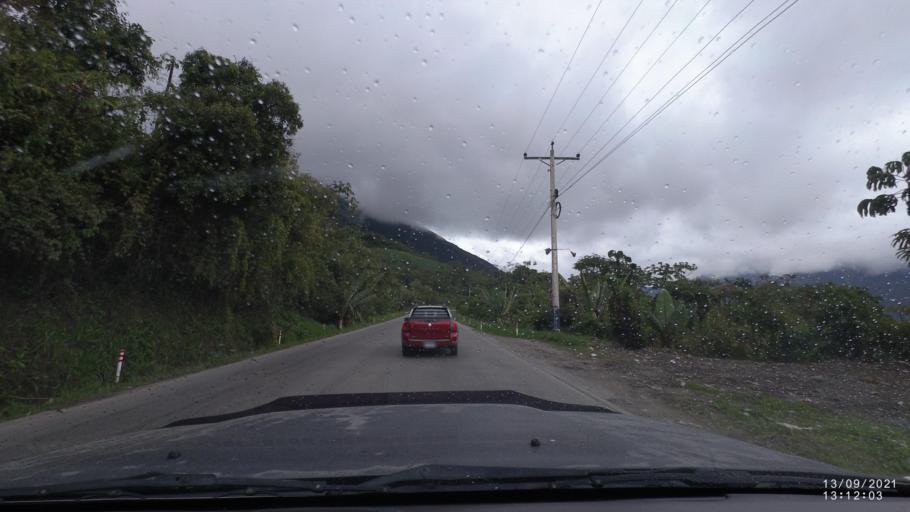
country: BO
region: Cochabamba
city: Colomi
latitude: -17.2011
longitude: -65.8341
